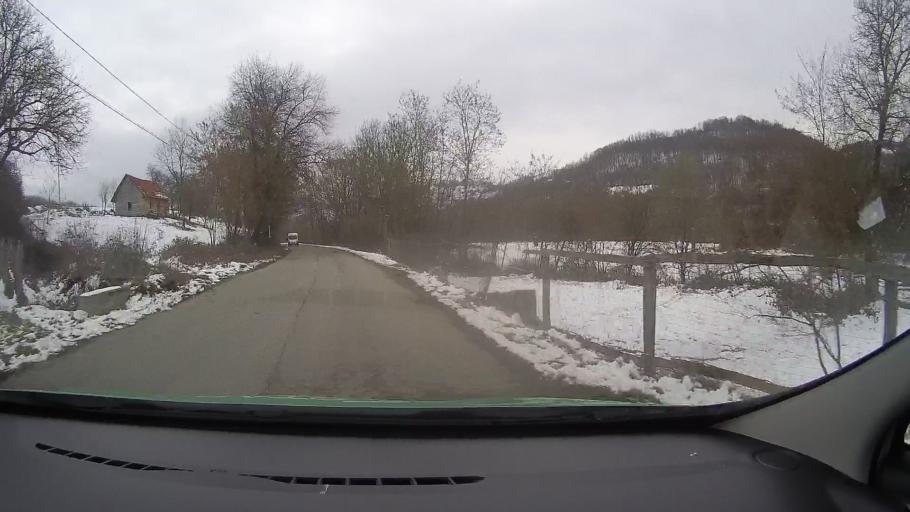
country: RO
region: Hunedoara
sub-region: Comuna Balsa
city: Balsa
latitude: 46.0364
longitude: 23.0785
